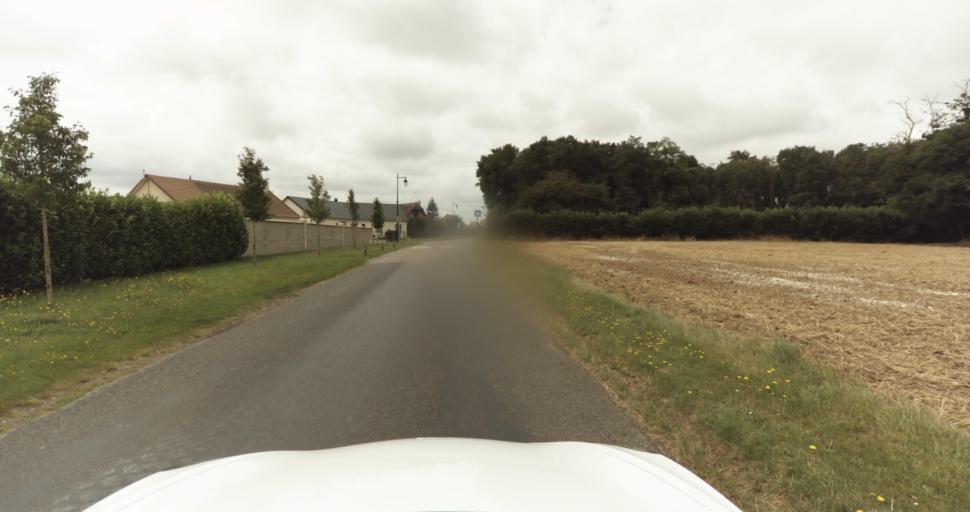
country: FR
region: Haute-Normandie
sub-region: Departement de l'Eure
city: Claville
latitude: 49.0291
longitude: 1.0464
